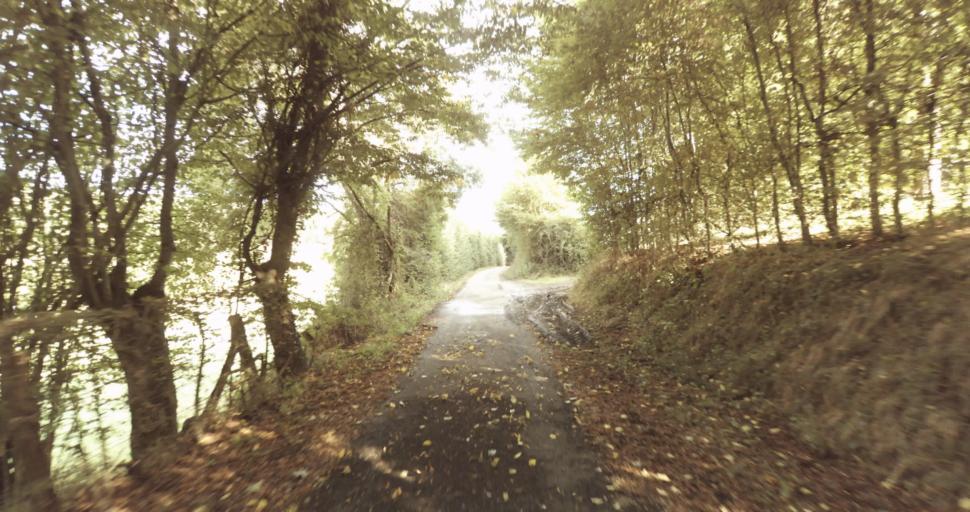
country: FR
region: Lower Normandy
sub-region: Departement de l'Orne
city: Gace
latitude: 48.8276
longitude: 0.2220
